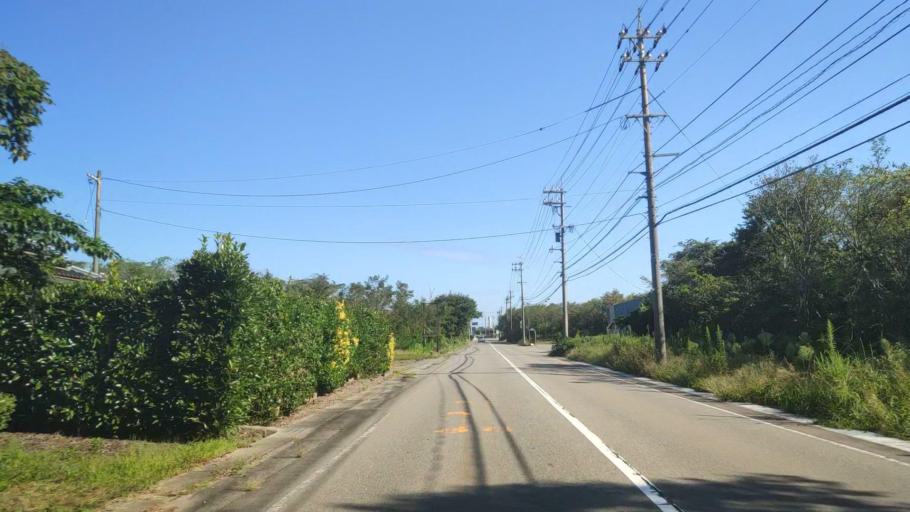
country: JP
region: Ishikawa
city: Hakui
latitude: 36.9752
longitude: 136.7755
